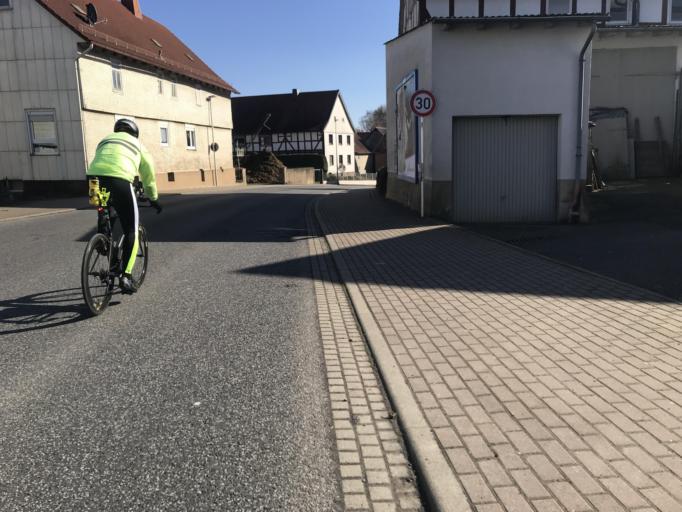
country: DE
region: Hesse
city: Schwalmstadt
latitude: 50.9053
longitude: 9.2114
